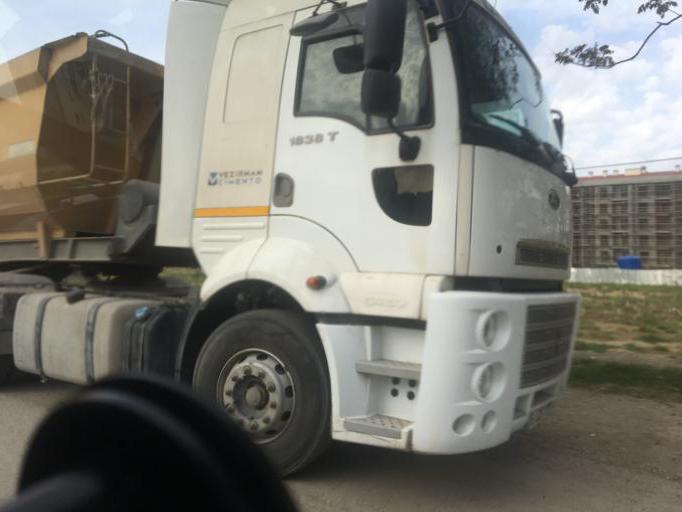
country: TR
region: Bursa
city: Yildirim
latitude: 40.2098
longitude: 29.0421
